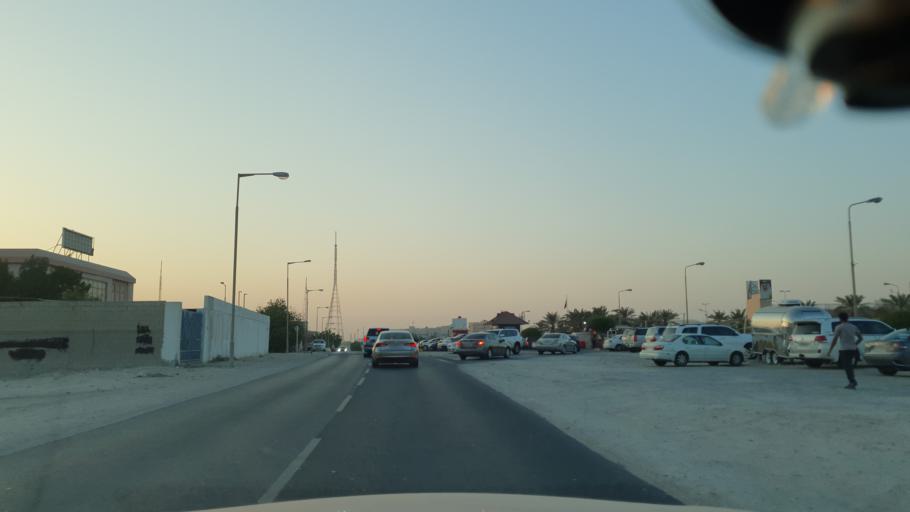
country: BH
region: Northern
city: Madinat `Isa
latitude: 26.1575
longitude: 50.5655
